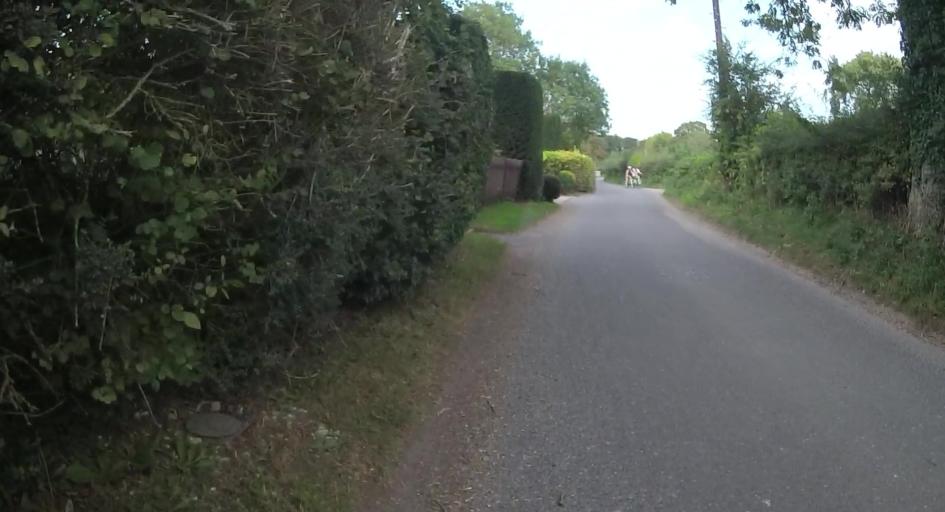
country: GB
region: England
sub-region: Hampshire
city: Kings Worthy
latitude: 51.0712
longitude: -1.1854
